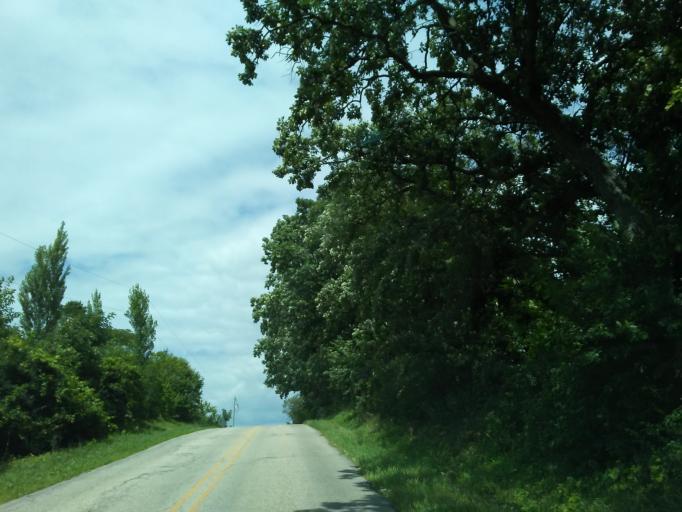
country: US
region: Wisconsin
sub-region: Dane County
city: Verona
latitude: 43.0038
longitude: -89.5782
